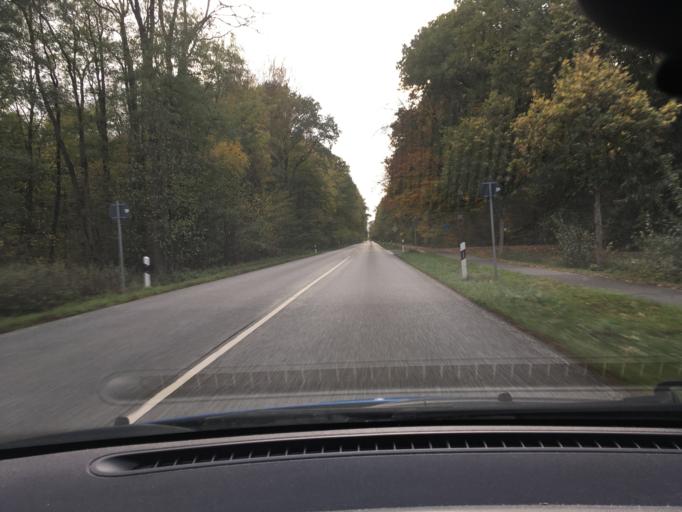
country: DE
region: Schleswig-Holstein
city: Elmenhorst
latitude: 53.5401
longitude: 10.5321
